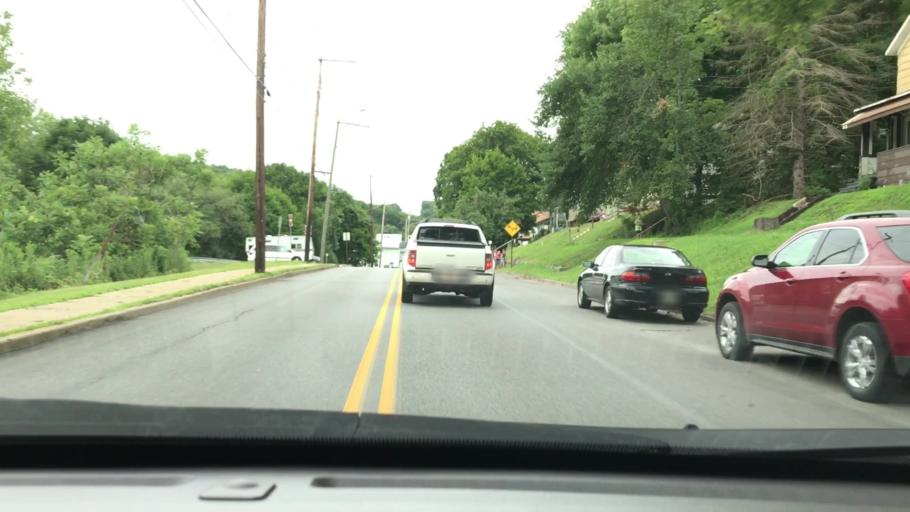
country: US
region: Pennsylvania
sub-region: Elk County
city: Ridgway
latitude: 41.4321
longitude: -78.7345
